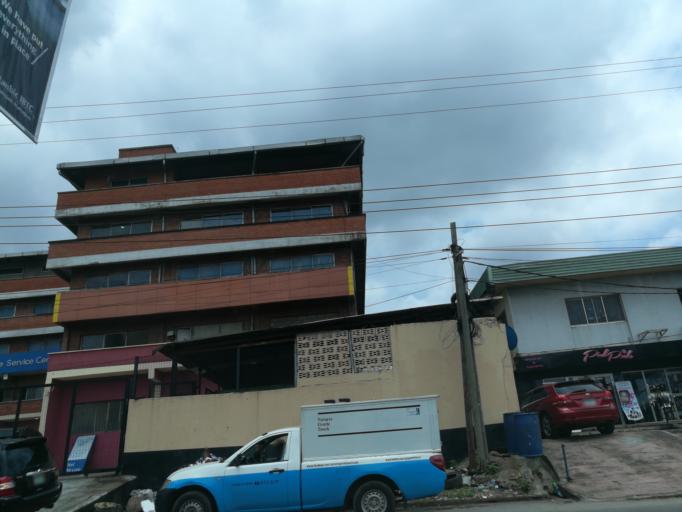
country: NG
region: Lagos
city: Ojota
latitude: 6.5876
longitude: 3.3628
